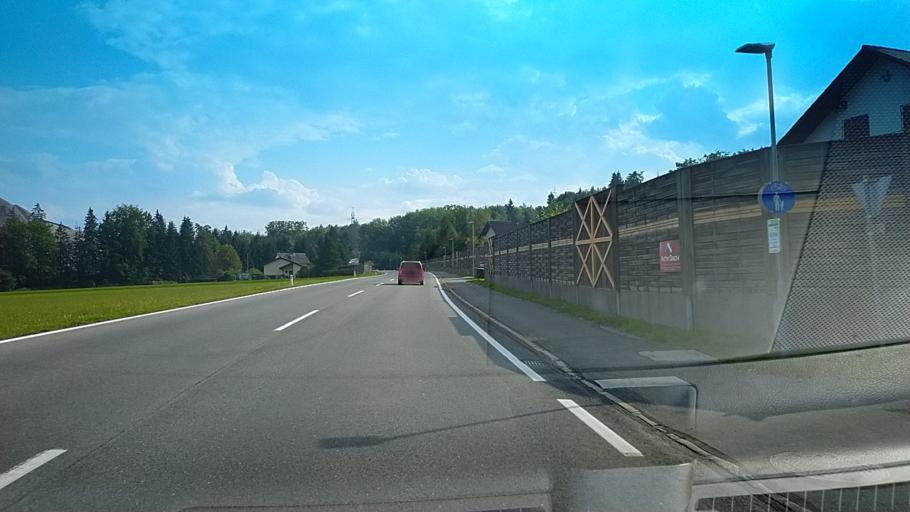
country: AT
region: Styria
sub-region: Politischer Bezirk Deutschlandsberg
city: Hollenegg
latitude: 46.7984
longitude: 15.2202
